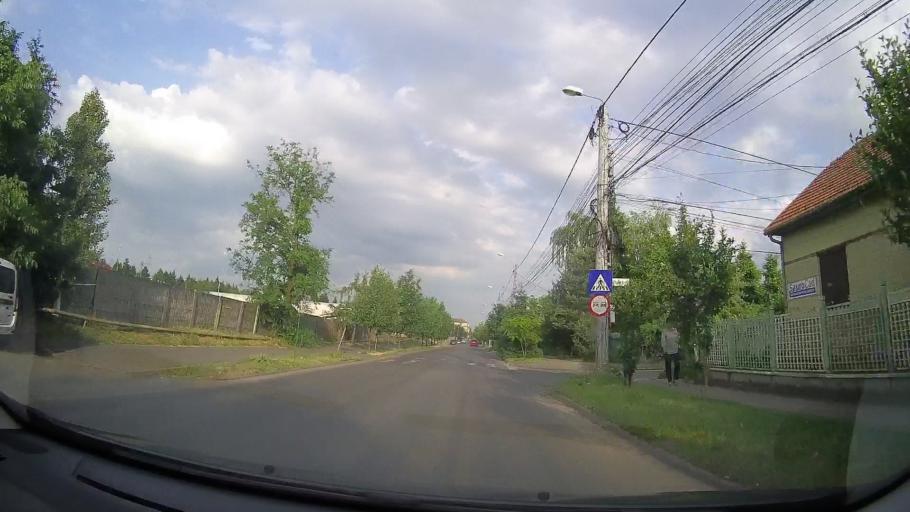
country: RO
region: Timis
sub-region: Comuna Dumbravita
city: Dumbravita
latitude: 45.7780
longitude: 21.2299
